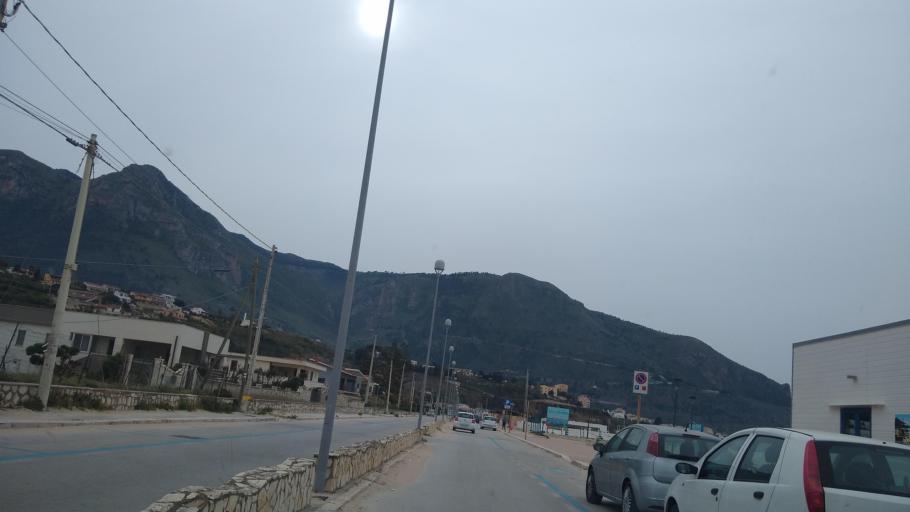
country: IT
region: Sicily
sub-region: Trapani
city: Castellammare del Golfo
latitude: 38.0238
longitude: 12.9019
